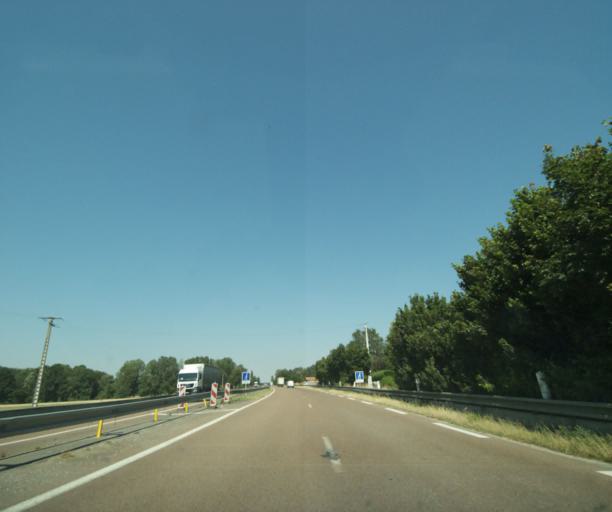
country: FR
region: Champagne-Ardenne
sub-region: Departement de la Marne
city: Frignicourt
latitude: 48.6882
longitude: 4.7269
